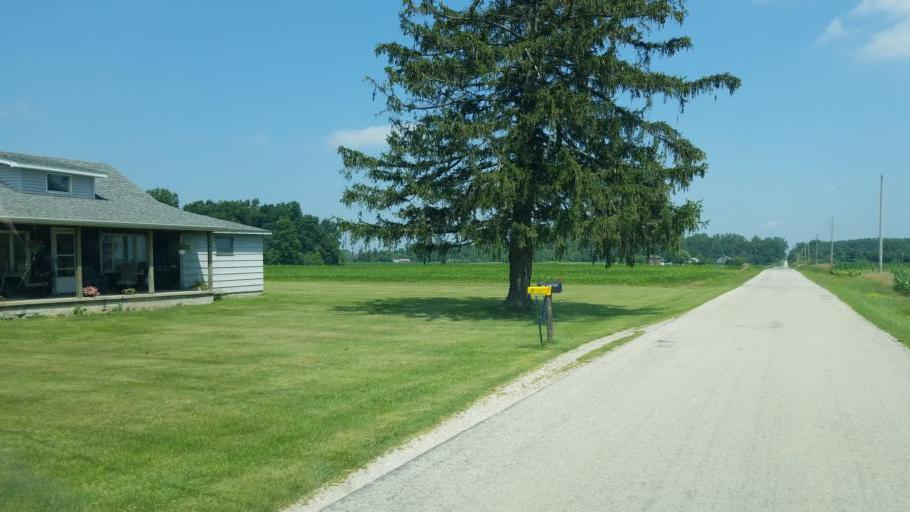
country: US
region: Ohio
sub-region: Seneca County
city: Tiffin
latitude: 41.0464
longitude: -82.9772
